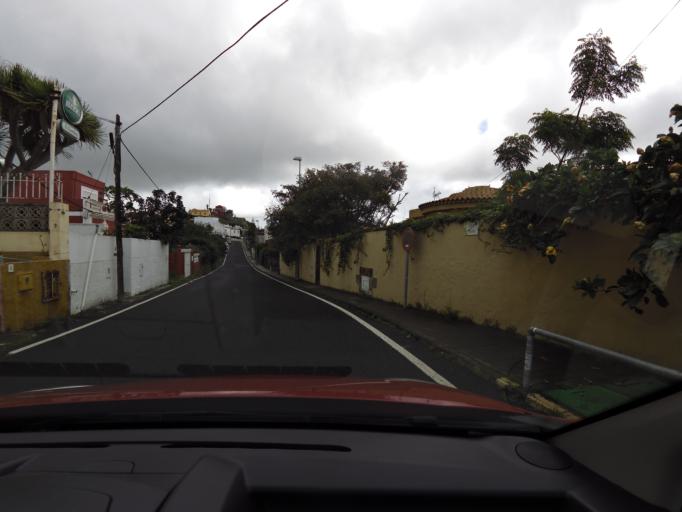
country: ES
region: Canary Islands
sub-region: Provincia de Las Palmas
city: Santa Brigida
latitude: 28.0309
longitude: -15.4713
